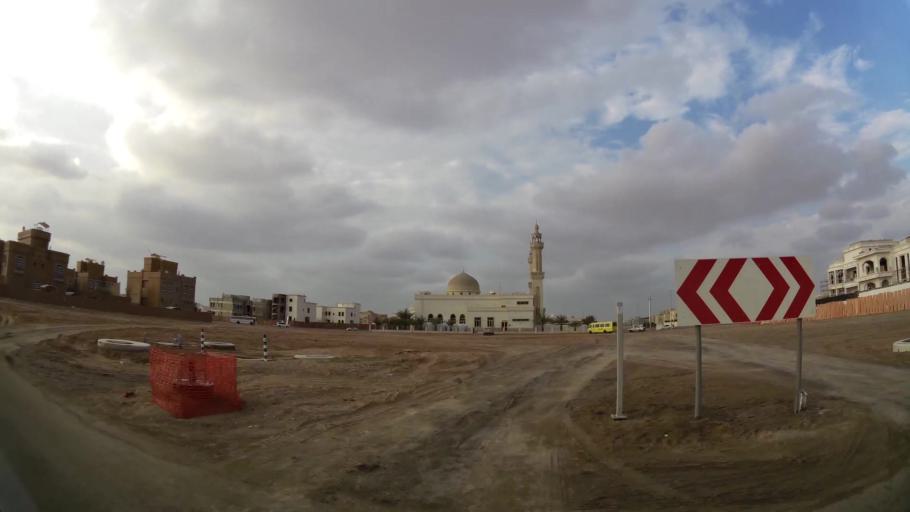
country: AE
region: Abu Dhabi
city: Abu Dhabi
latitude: 24.3517
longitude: 54.5590
